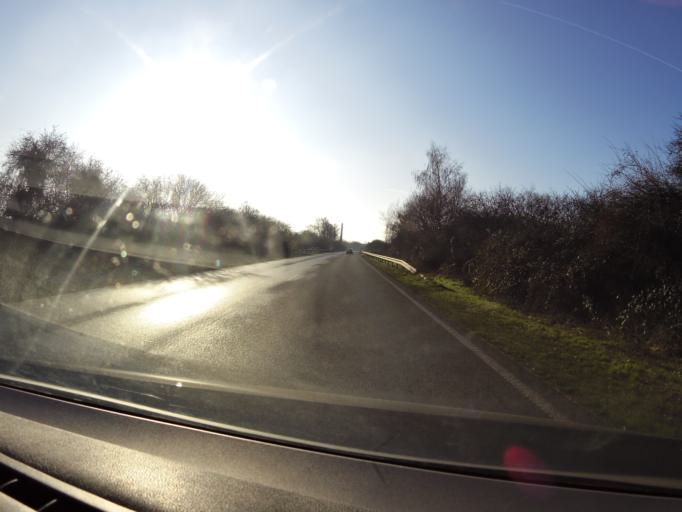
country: DE
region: North Rhine-Westphalia
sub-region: Regierungsbezirk Dusseldorf
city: Bruggen
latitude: 51.2894
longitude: 6.1908
